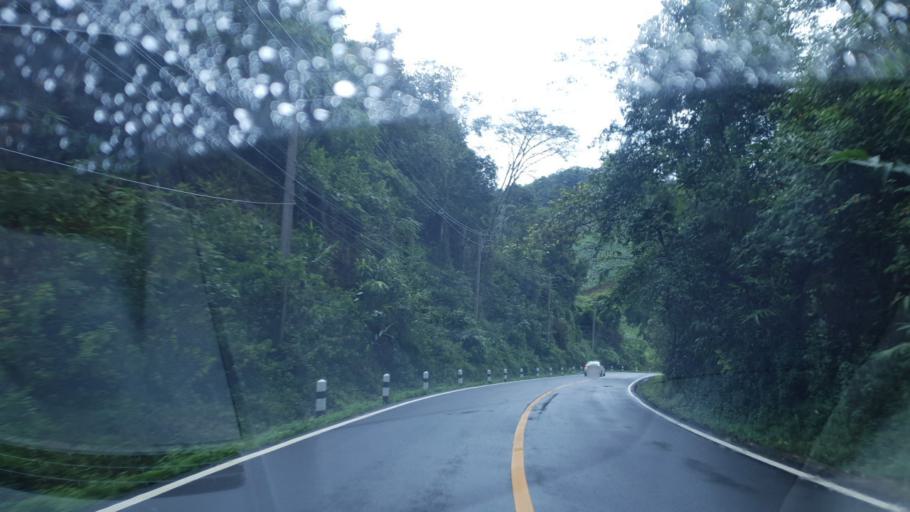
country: TH
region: Mae Hong Son
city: Ban Huai I Huak
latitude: 18.1437
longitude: 98.1144
